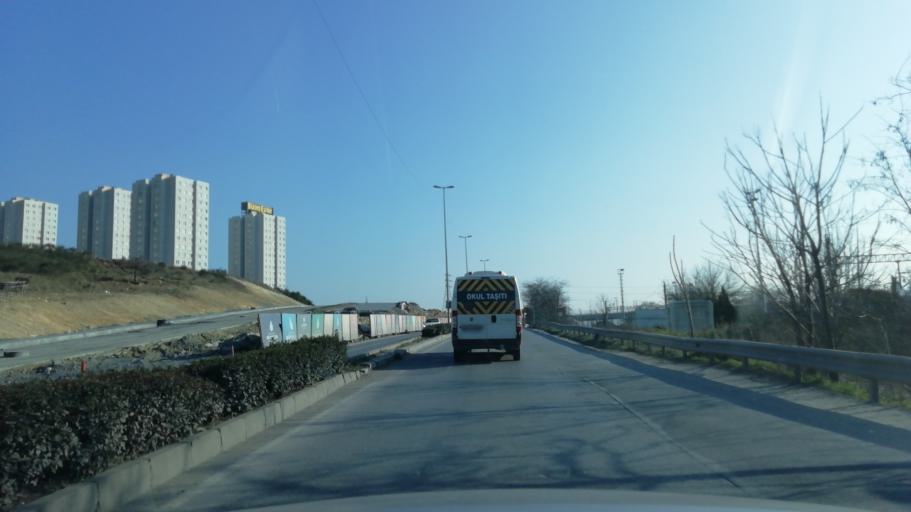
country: TR
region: Istanbul
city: Esenyurt
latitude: 41.0633
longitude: 28.6998
